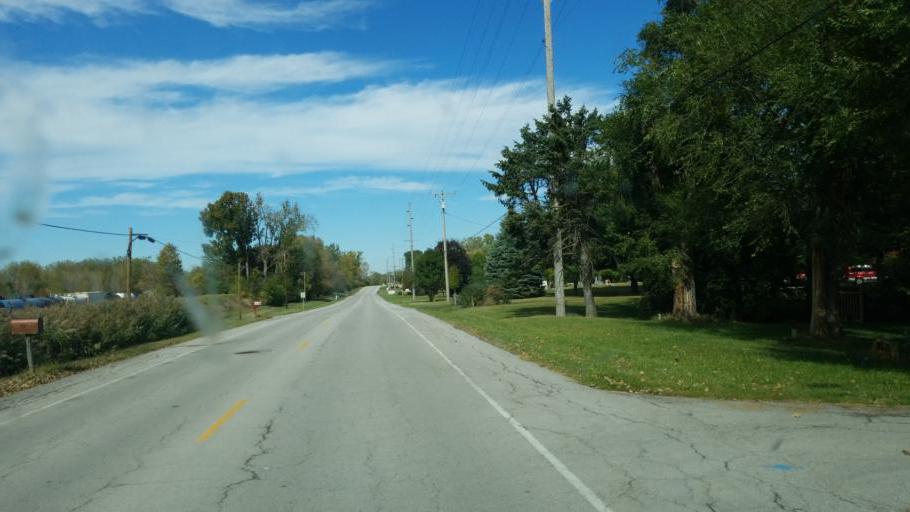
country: US
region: Ohio
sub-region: Erie County
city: Huron
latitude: 41.3746
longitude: -82.5454
